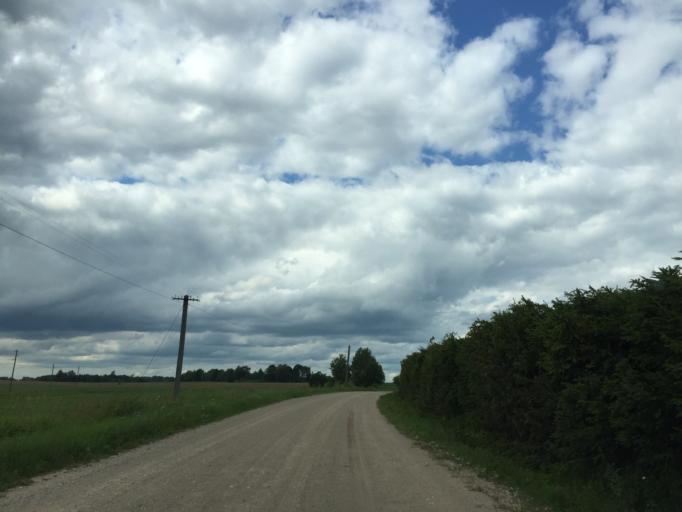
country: LV
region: Malpils
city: Malpils
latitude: 56.8466
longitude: 25.0497
